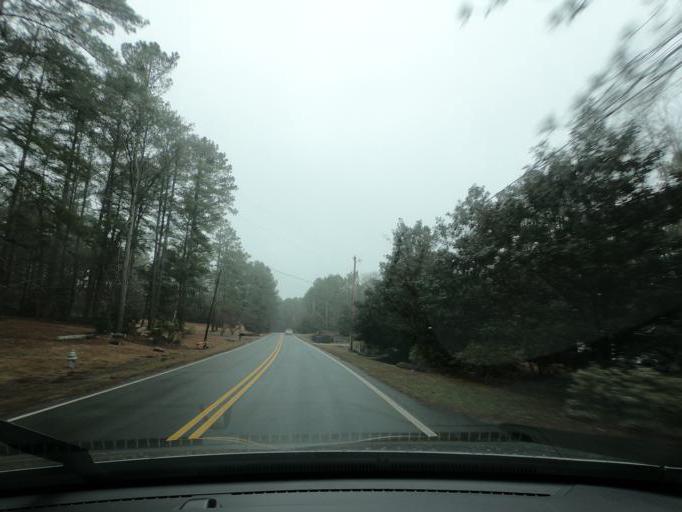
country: US
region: Georgia
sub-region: Fulton County
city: Milton
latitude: 34.1199
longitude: -84.3052
